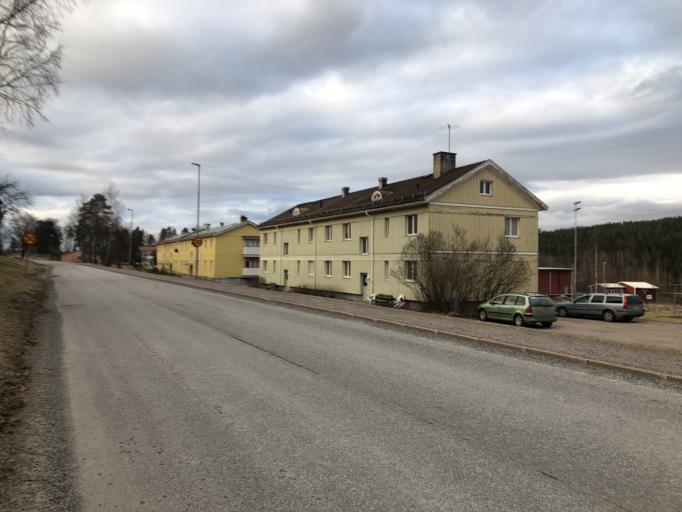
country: SE
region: Vaermland
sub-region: Filipstads Kommun
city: Lesjofors
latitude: 59.9826
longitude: 14.1751
